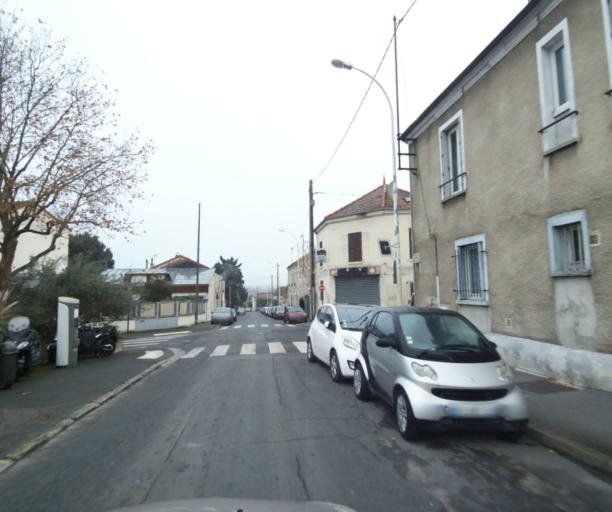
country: FR
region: Ile-de-France
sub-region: Departement de Seine-Saint-Denis
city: Neuilly-Plaisance
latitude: 48.8617
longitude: 2.5041
